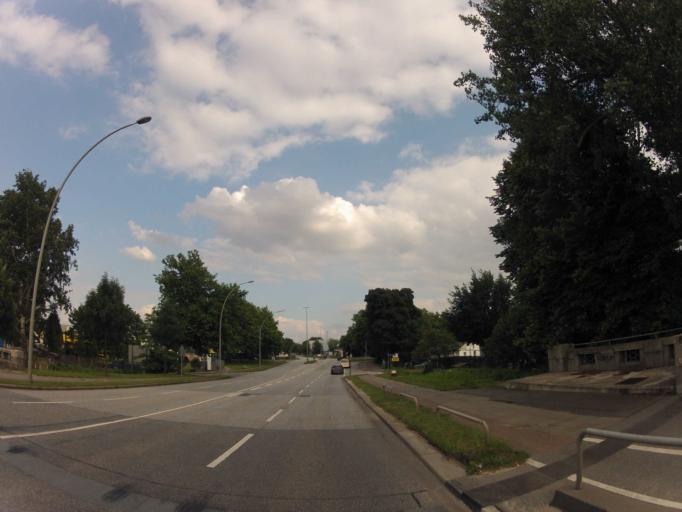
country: DE
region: Hamburg
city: Rothenburgsort
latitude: 53.5431
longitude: 10.0419
